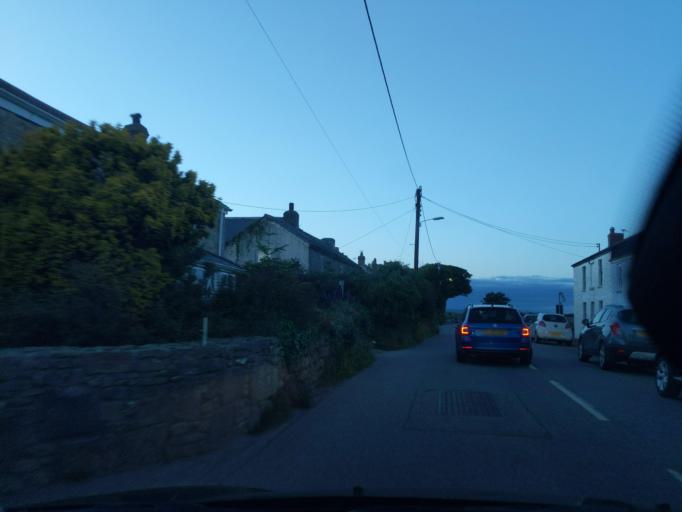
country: GB
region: England
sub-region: Cornwall
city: St. Buryan
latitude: 50.0762
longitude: -5.6209
